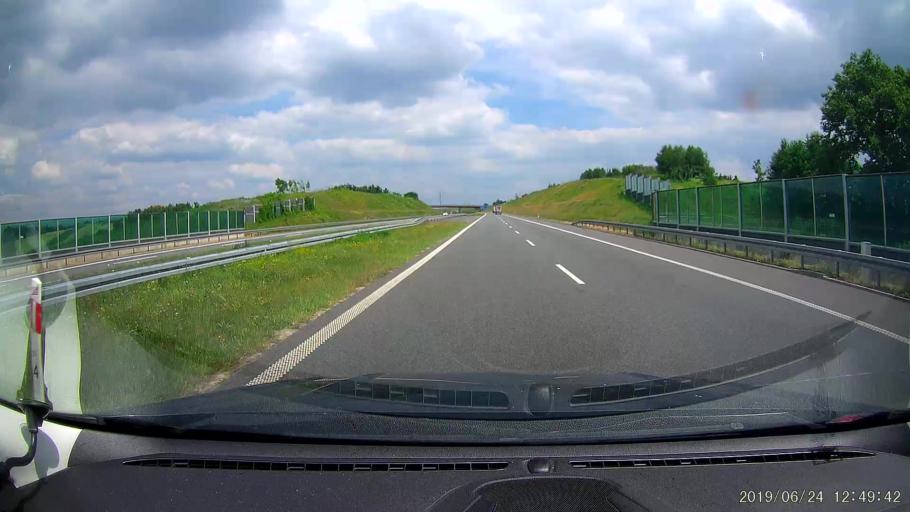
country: PL
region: Silesian Voivodeship
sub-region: Powiat rybnicki
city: Swierklany Gorne
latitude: 50.0159
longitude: 18.5931
